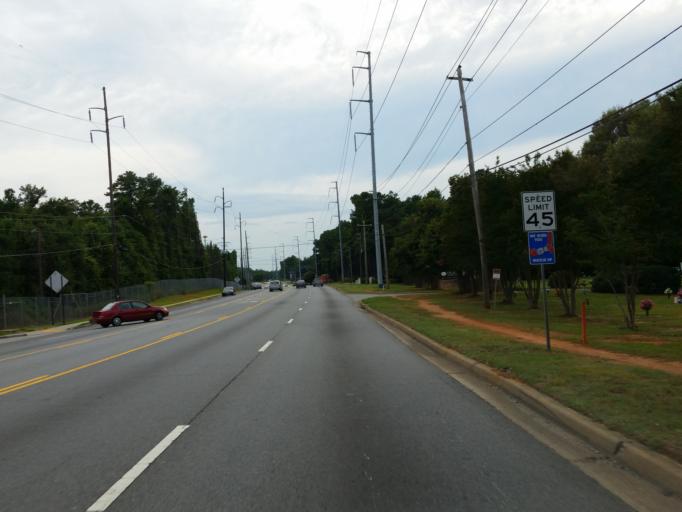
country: US
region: Georgia
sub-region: Cobb County
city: Smyrna
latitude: 33.9012
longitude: -84.4907
